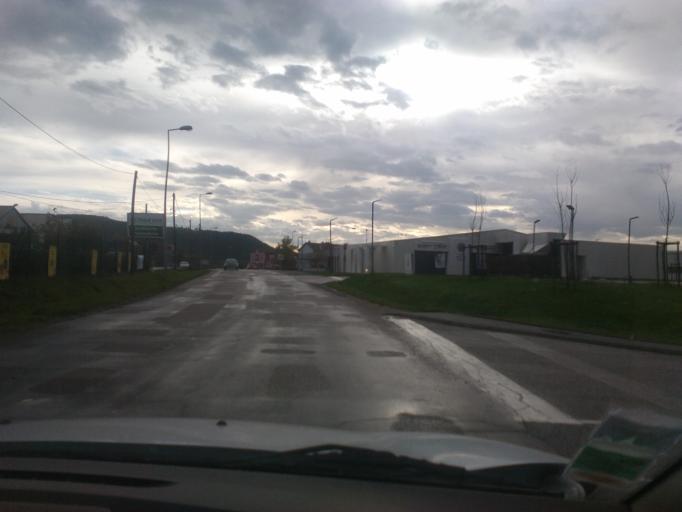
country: FR
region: Lorraine
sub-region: Departement des Vosges
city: Bruyeres
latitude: 48.2031
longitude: 6.7208
